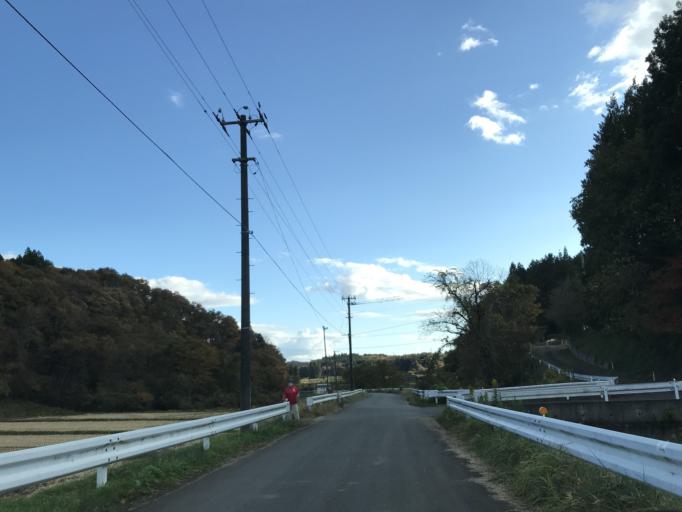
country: JP
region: Iwate
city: Ichinoseki
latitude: 38.8649
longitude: 141.1382
